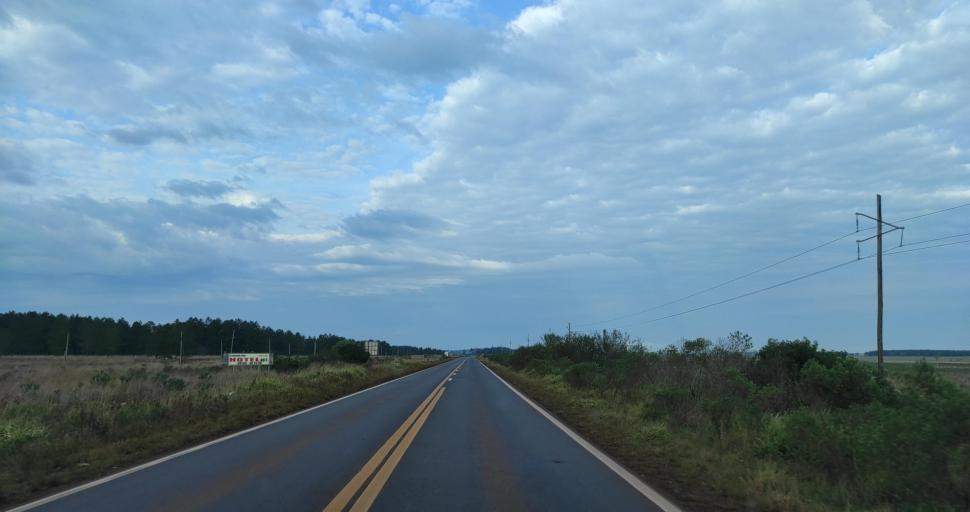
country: AR
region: Corrientes
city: San Carlos
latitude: -27.8917
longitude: -55.9354
